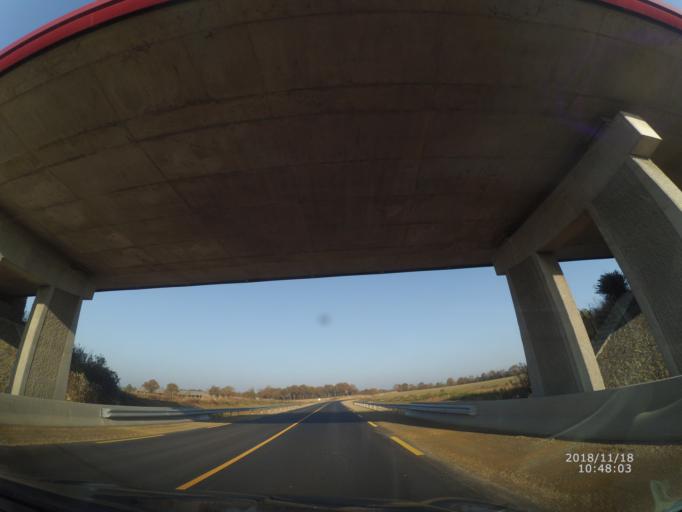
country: FR
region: Pays de la Loire
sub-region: Departement de la Loire-Atlantique
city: Vue
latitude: 47.1998
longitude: -1.9180
